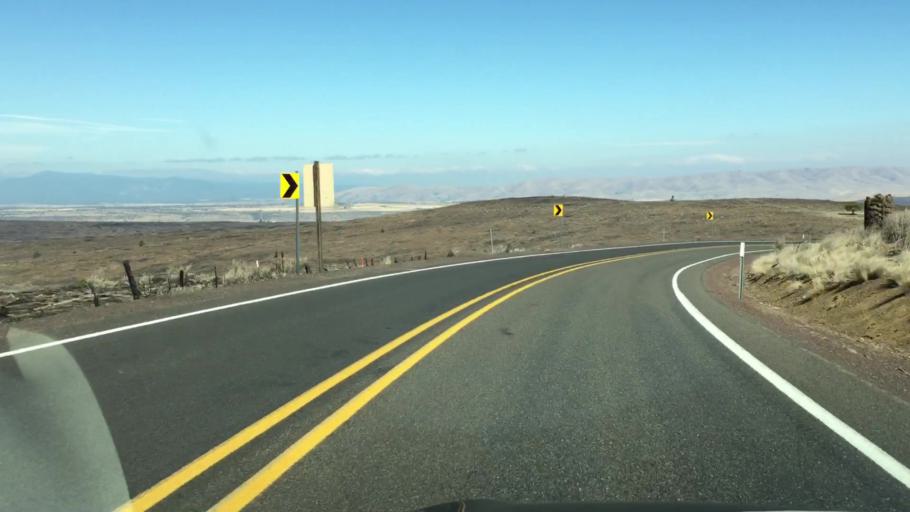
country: US
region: Oregon
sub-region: Jefferson County
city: Warm Springs
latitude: 45.1098
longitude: -121.0417
